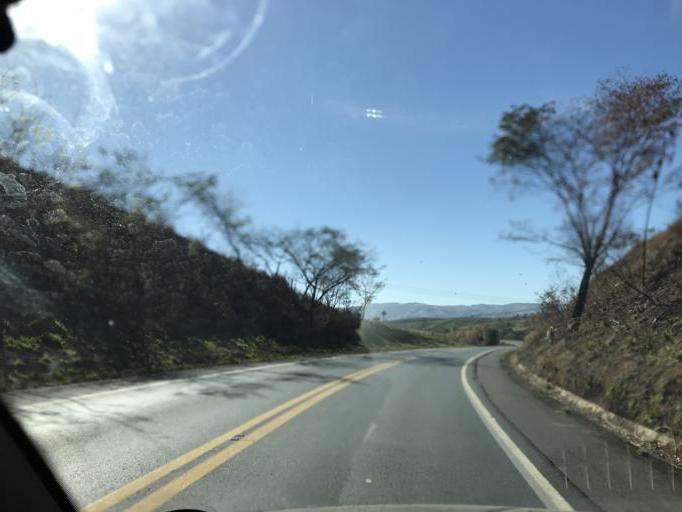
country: BR
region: Minas Gerais
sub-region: Bambui
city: Bambui
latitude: -19.8453
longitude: -45.9997
